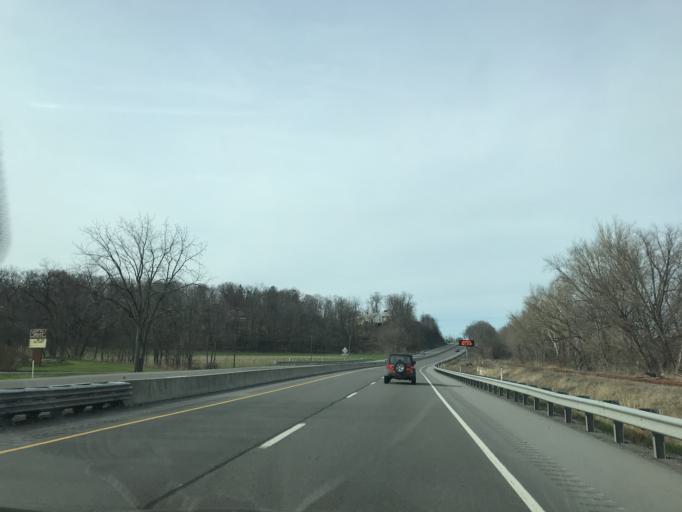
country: US
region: Pennsylvania
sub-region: Northumberland County
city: Milton
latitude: 41.0068
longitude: -76.8680
